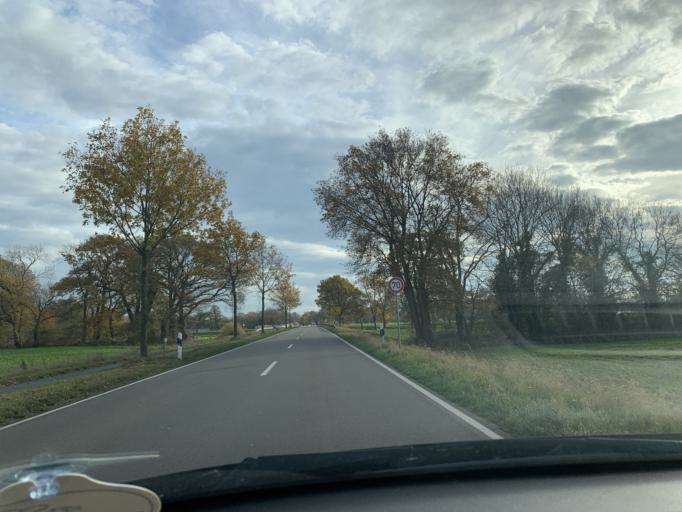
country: DE
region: Lower Saxony
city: Apen
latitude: 53.2131
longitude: 7.8099
